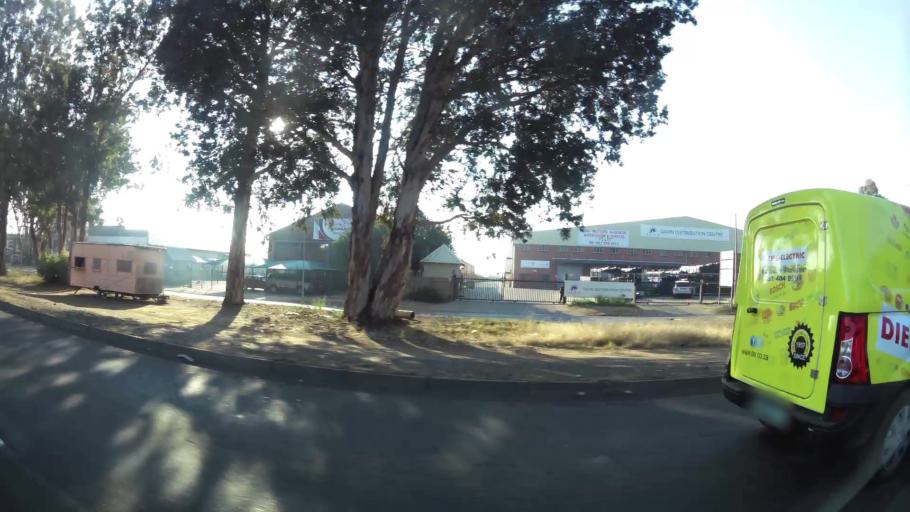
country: ZA
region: Orange Free State
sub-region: Mangaung Metropolitan Municipality
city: Bloemfontein
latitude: -29.1551
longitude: 26.2182
